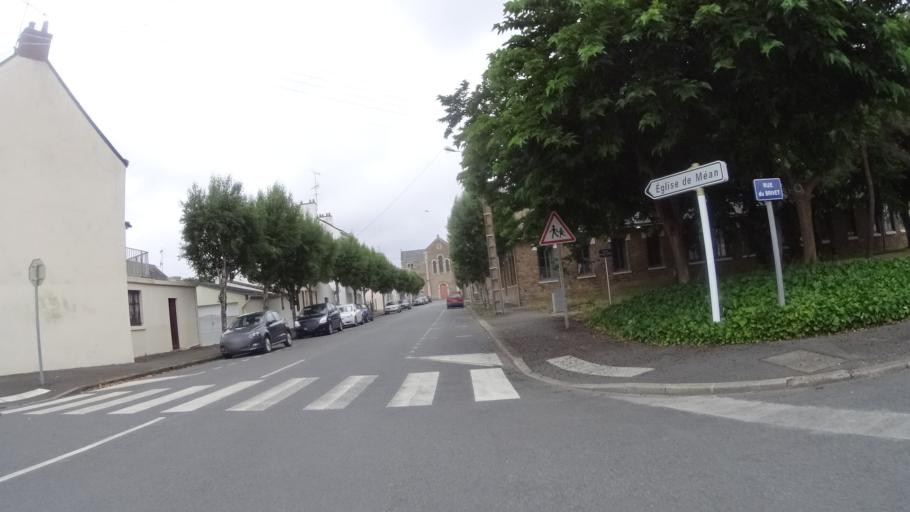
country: FR
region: Pays de la Loire
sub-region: Departement de la Loire-Atlantique
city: Trignac
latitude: 47.2985
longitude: -2.1856
